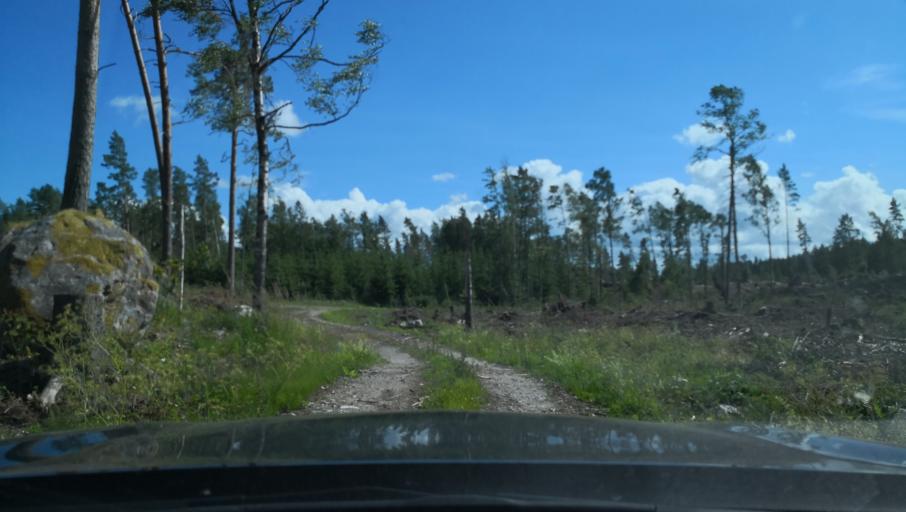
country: SE
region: Vaestmanland
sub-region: Kungsors Kommun
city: Kungsoer
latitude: 59.3370
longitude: 16.0650
